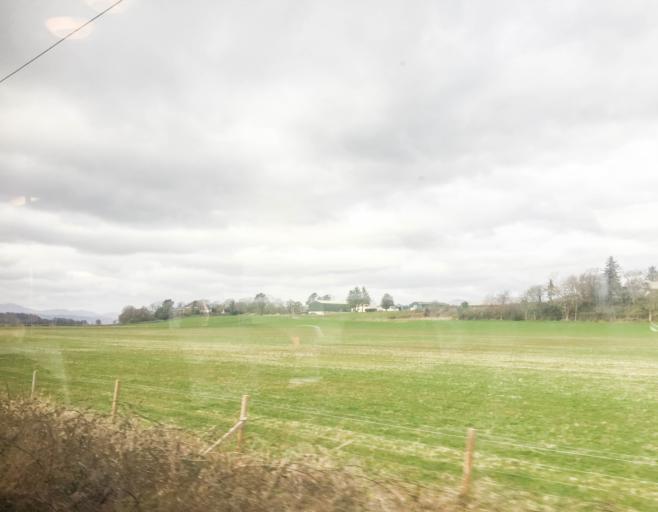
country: GB
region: Scotland
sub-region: Argyll and Bute
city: Cardross
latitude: 55.9622
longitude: -4.6655
